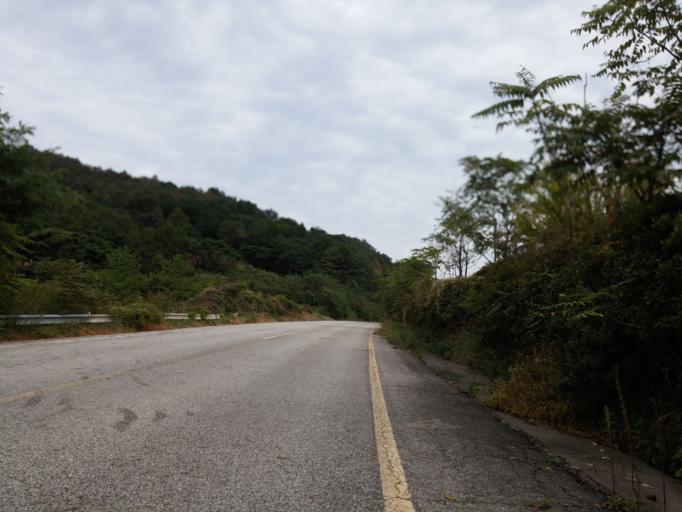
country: KR
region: Chungcheongnam-do
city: Yonmu
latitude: 36.1645
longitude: 127.1905
